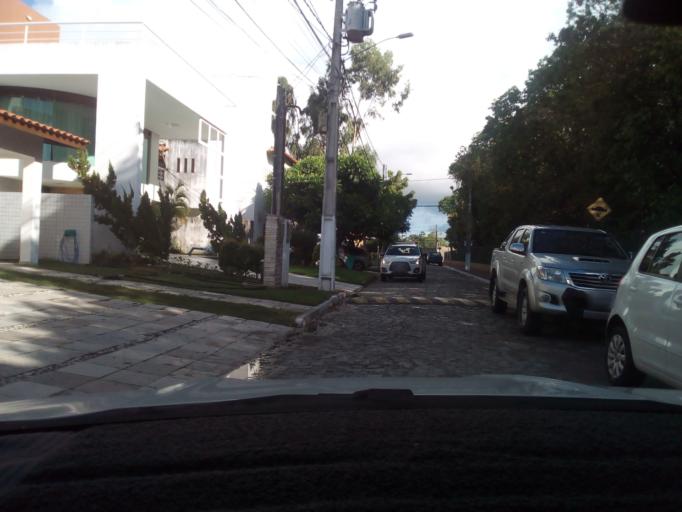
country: BR
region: Paraiba
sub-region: Joao Pessoa
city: Joao Pessoa
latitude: -7.1405
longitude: -34.8232
